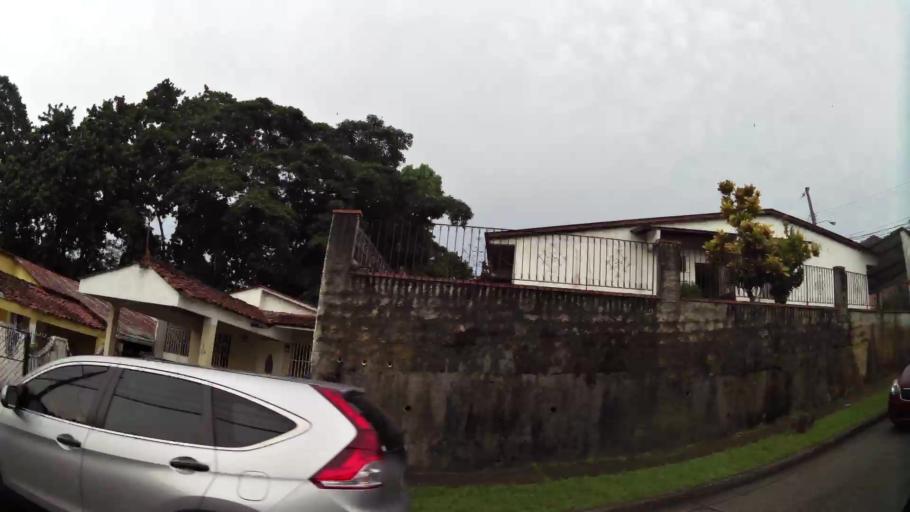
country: PA
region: Panama
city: Panama
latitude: 9.0122
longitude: -79.5402
